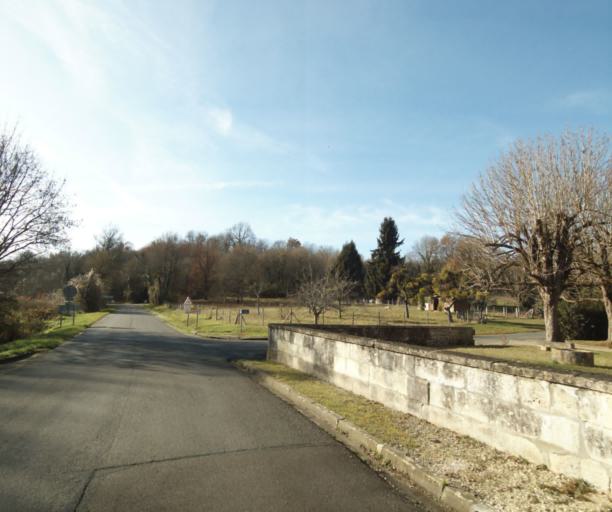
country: FR
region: Poitou-Charentes
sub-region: Departement de la Charente-Maritime
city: Chaniers
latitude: 45.7503
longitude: -0.5087
